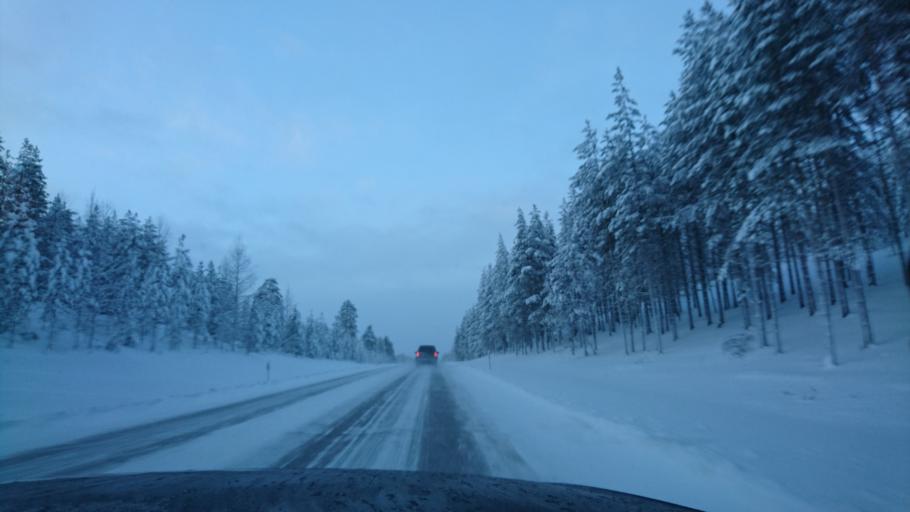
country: FI
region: Northern Ostrobothnia
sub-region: Koillismaa
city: Taivalkoski
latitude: 65.4684
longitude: 27.6846
